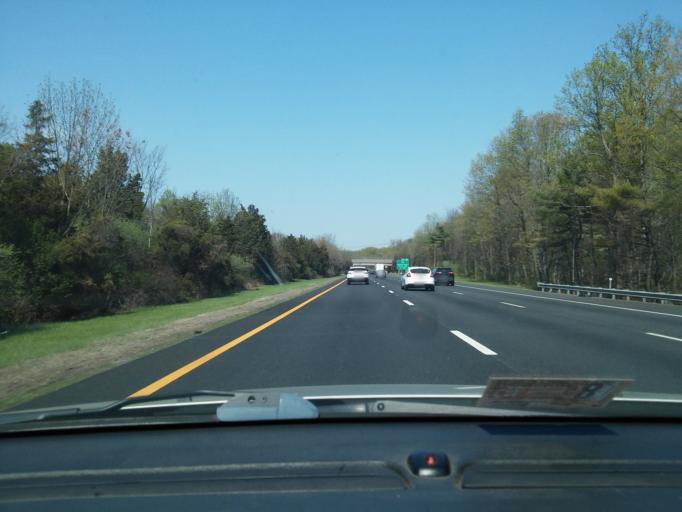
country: US
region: New Jersey
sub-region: Somerset County
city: Warren Township
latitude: 40.6474
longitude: -74.5091
